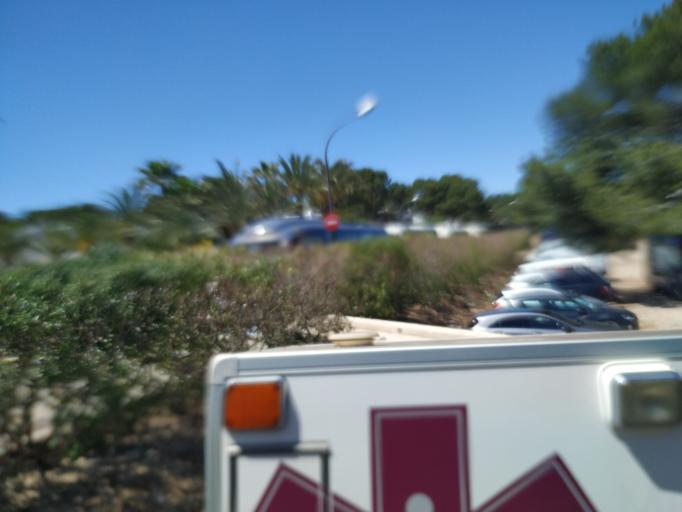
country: ES
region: Balearic Islands
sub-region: Illes Balears
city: Ibiza
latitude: 38.9143
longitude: 1.4695
